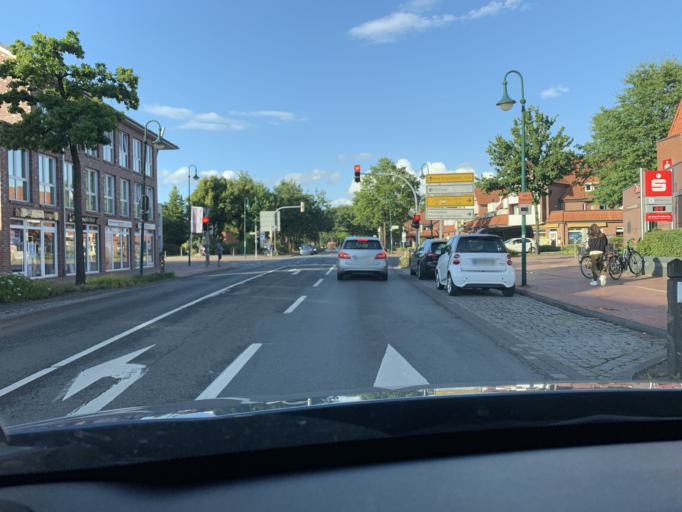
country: DE
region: Lower Saxony
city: Edewecht
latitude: 53.1277
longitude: 7.9840
